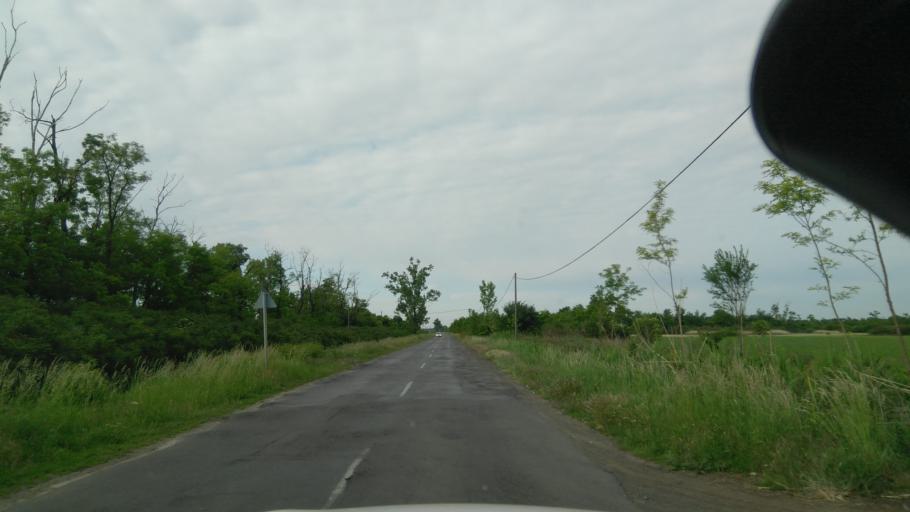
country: HU
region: Bekes
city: Elek
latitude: 46.5862
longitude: 21.2244
